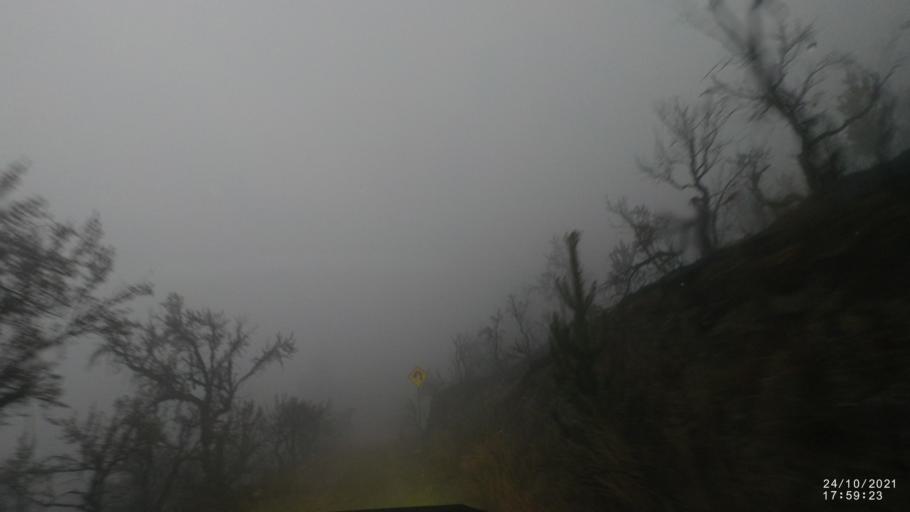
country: BO
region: Cochabamba
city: Cochabamba
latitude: -17.3255
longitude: -66.1312
